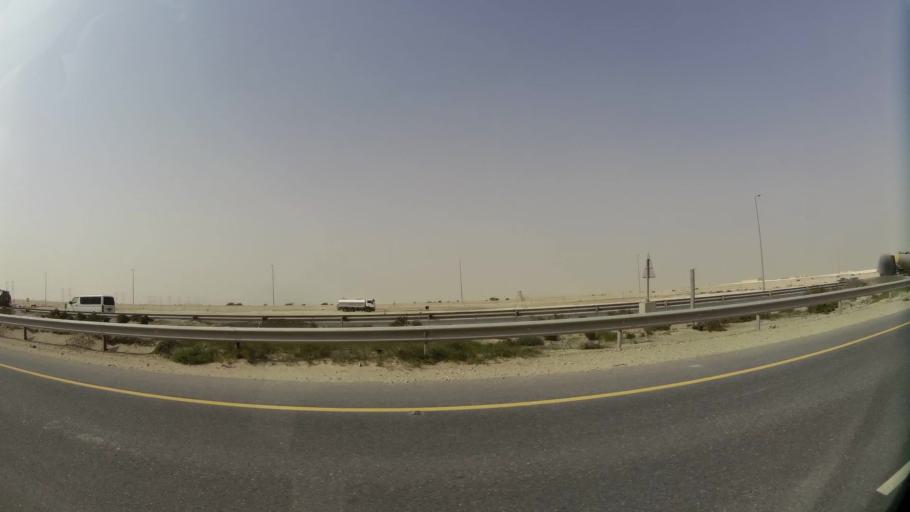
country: QA
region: Baladiyat ar Rayyan
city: Ar Rayyan
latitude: 25.1798
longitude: 51.3471
